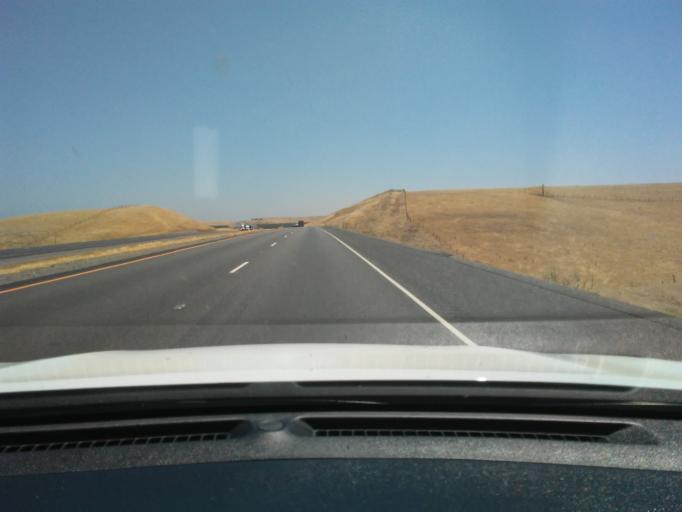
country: US
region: California
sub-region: Stanislaus County
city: Patterson
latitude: 37.4158
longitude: -121.1507
